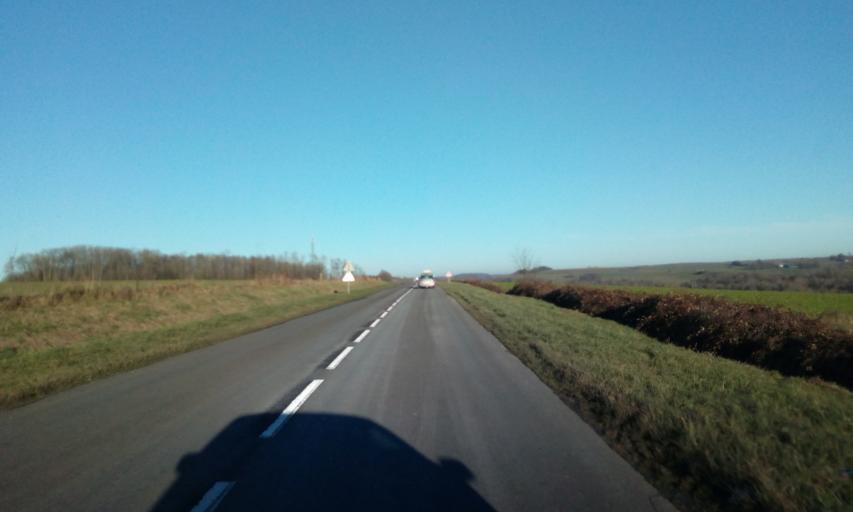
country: FR
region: Champagne-Ardenne
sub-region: Departement des Ardennes
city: Signy-le-Petit
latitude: 49.7483
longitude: 4.3047
